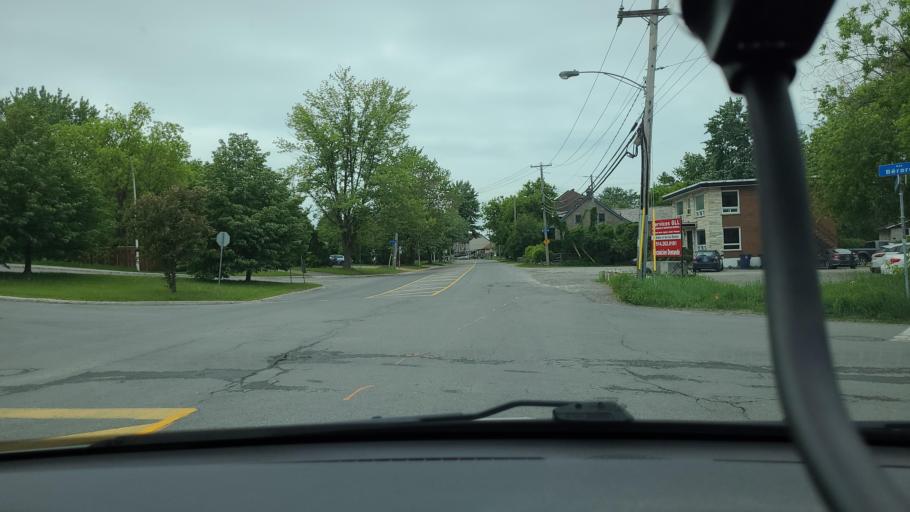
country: CA
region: Quebec
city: Bois-des-Filion
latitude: 45.6433
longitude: -73.7561
